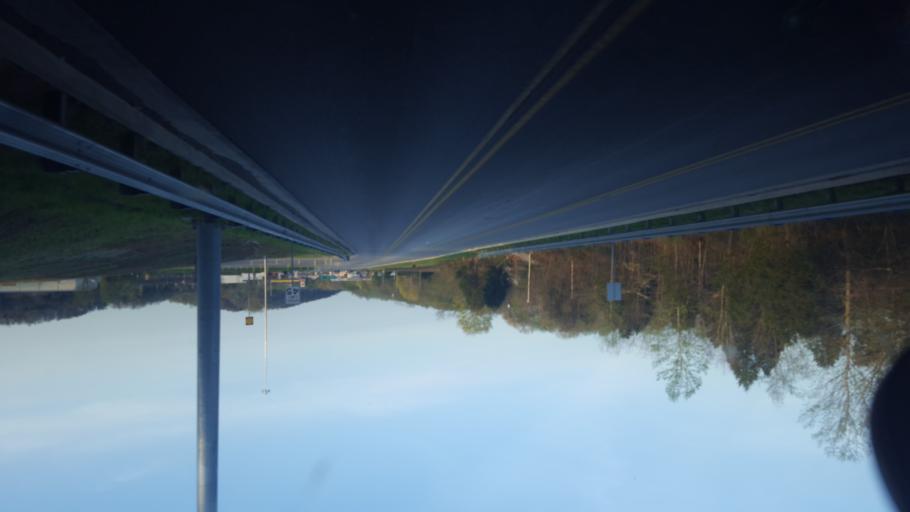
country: US
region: Kentucky
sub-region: Hart County
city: Munfordville
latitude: 37.2916
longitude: -85.9036
